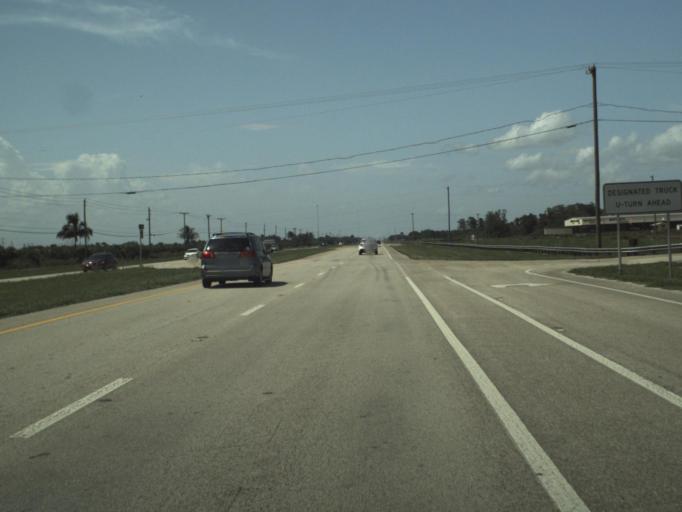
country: US
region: Florida
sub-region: Palm Beach County
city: Villages of Oriole
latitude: 26.5030
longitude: -80.2050
